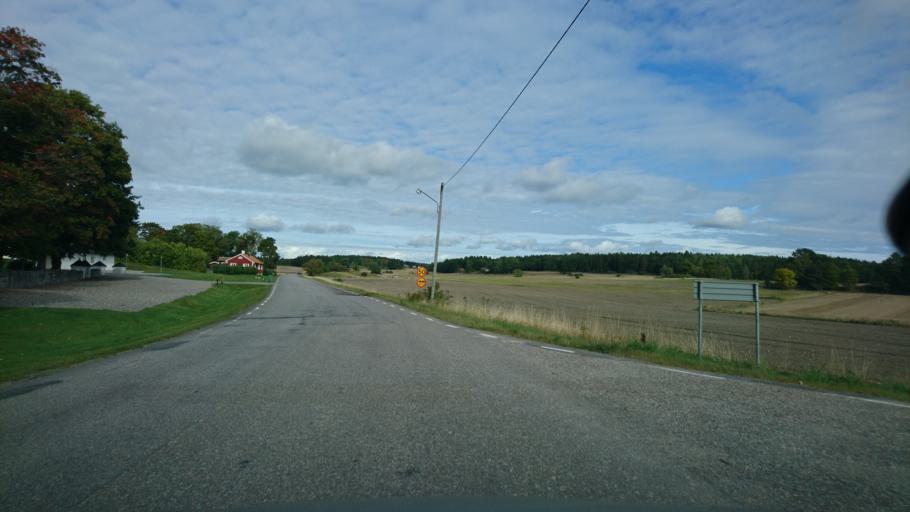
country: SE
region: Soedermanland
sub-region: Strangnas Kommun
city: Stallarholmen
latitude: 59.3763
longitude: 17.2580
